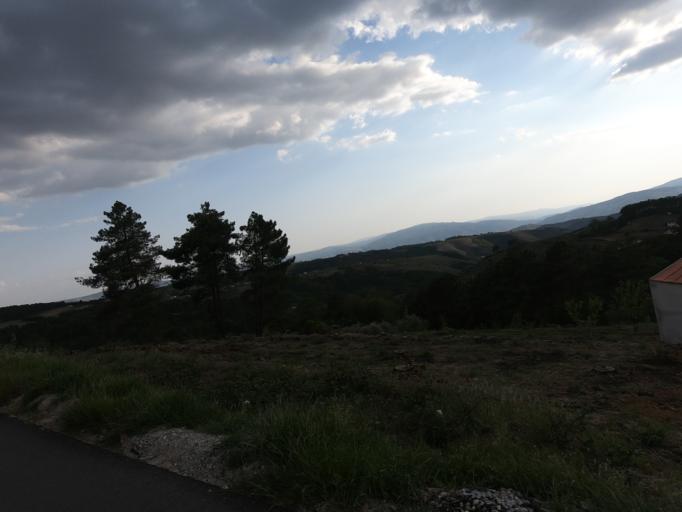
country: PT
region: Vila Real
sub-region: Sabrosa
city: Vilela
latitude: 41.2226
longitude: -7.6820
